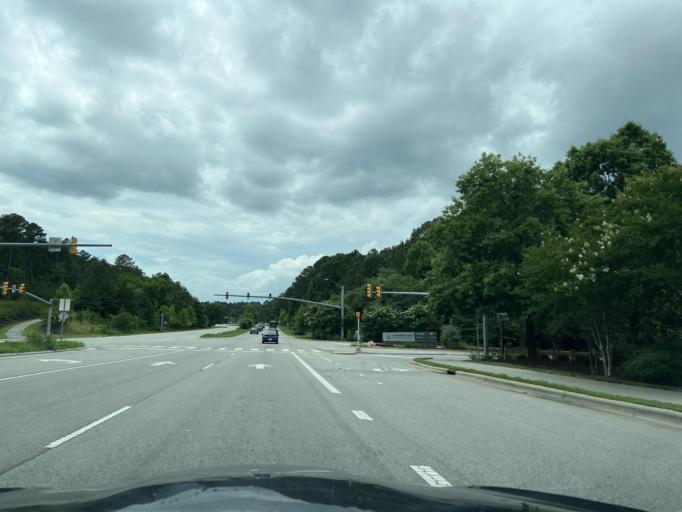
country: US
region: North Carolina
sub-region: Durham County
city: Durham
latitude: 35.9249
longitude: -78.8641
